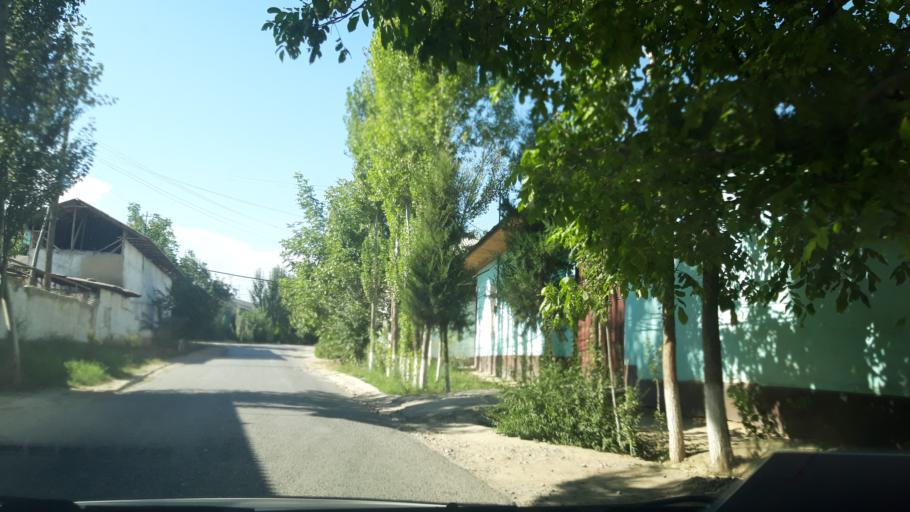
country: UZ
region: Namangan
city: Yangiqo`rg`on
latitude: 41.2054
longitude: 71.7264
